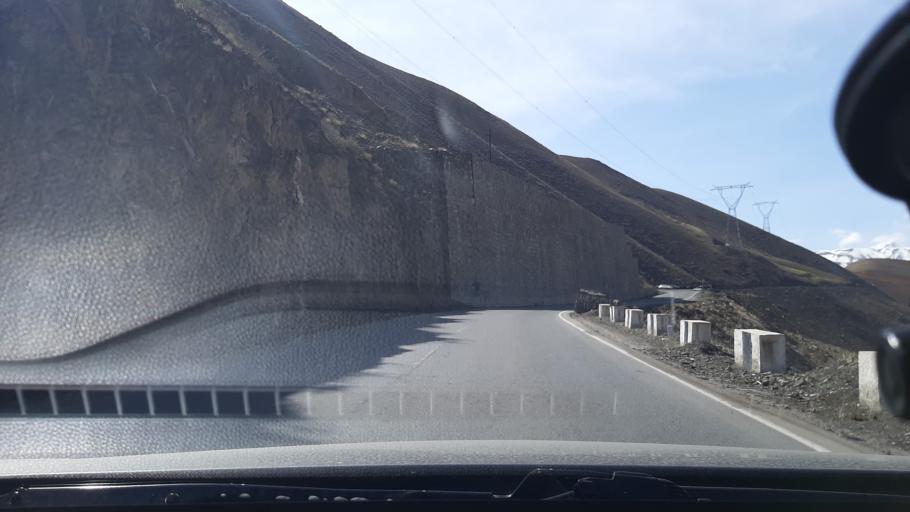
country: TJ
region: Viloyati Sughd
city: Ayni
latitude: 39.4384
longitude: 68.5476
